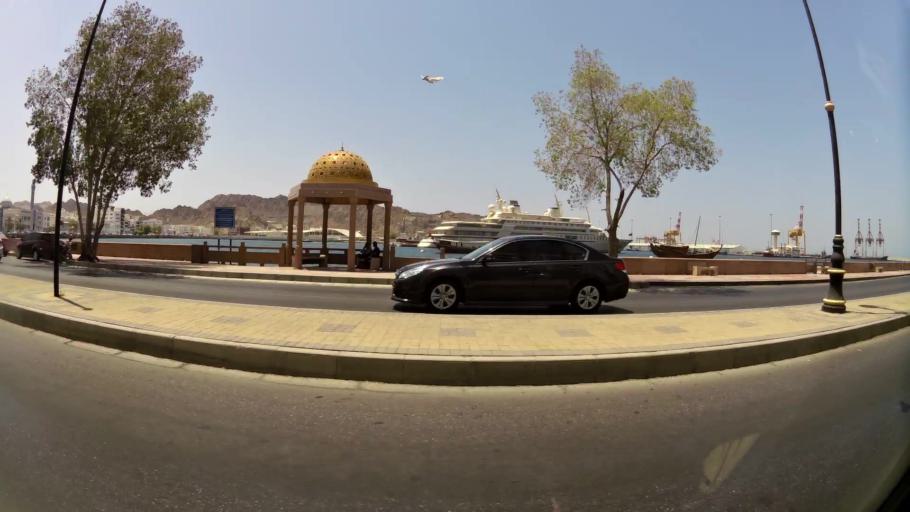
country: OM
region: Muhafazat Masqat
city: Muscat
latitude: 23.6218
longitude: 58.5669
